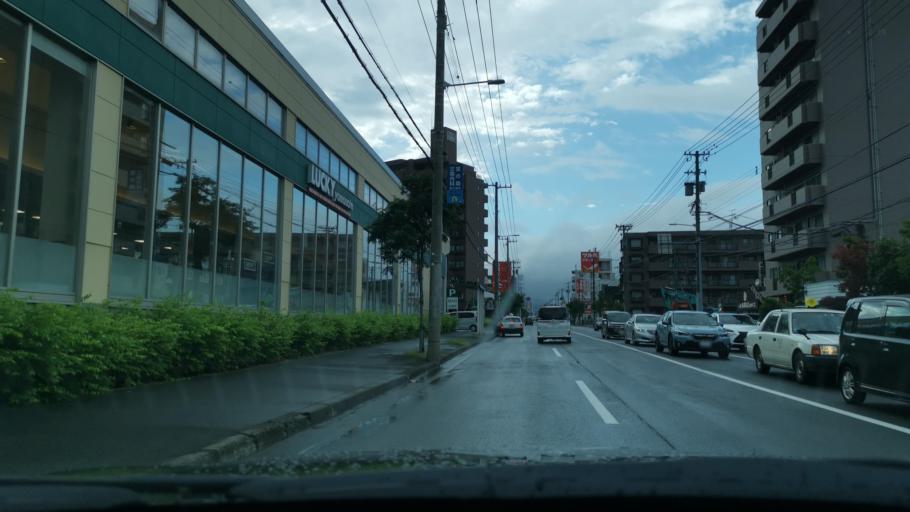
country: JP
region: Hokkaido
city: Sapporo
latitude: 43.0646
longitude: 141.3006
